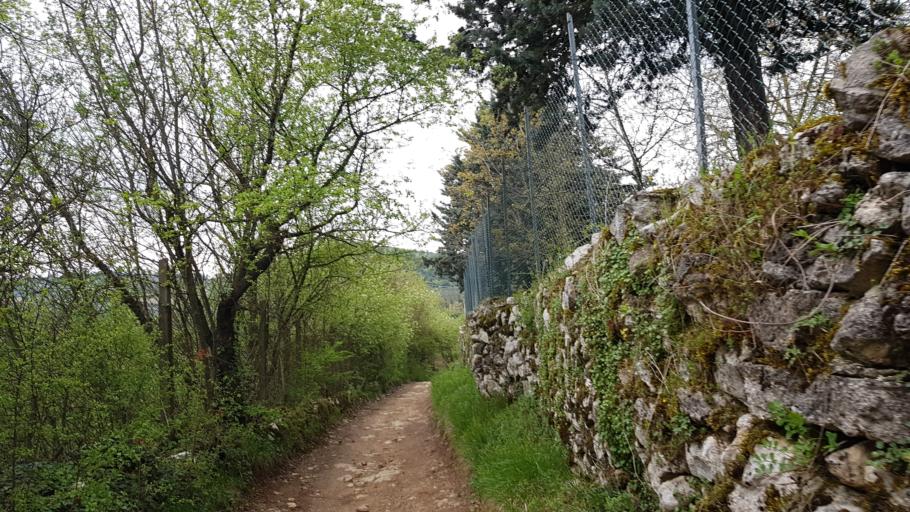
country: IT
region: Veneto
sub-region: Provincia di Verona
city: Parona
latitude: 45.4768
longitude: 10.9662
